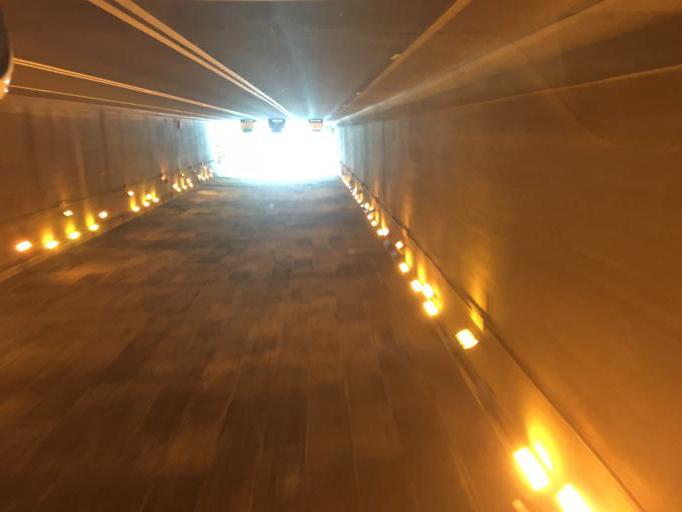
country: TW
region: Taiwan
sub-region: Chiayi
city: Jiayi Shi
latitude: 23.5766
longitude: 120.5078
